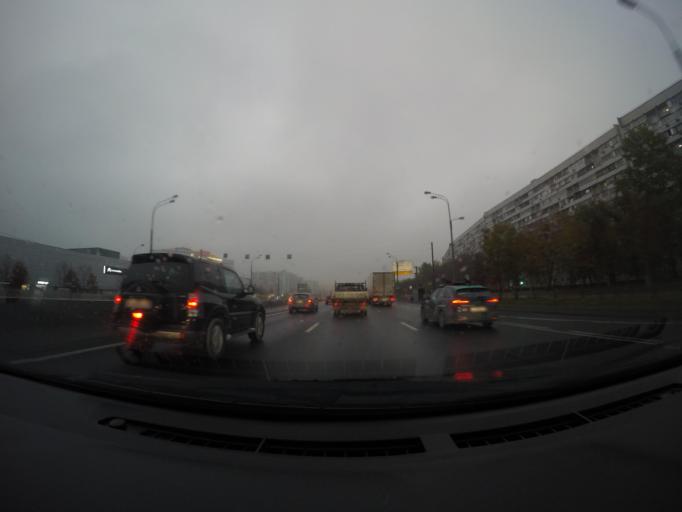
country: RU
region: Moscow
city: Chertanovo Yuzhnoye
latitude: 55.5988
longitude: 37.6037
